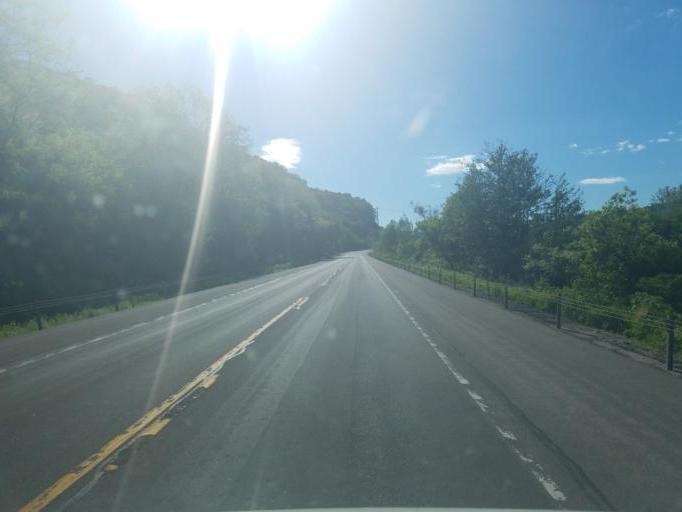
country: US
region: New York
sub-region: Herkimer County
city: Little Falls
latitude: 43.0357
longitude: -74.8382
